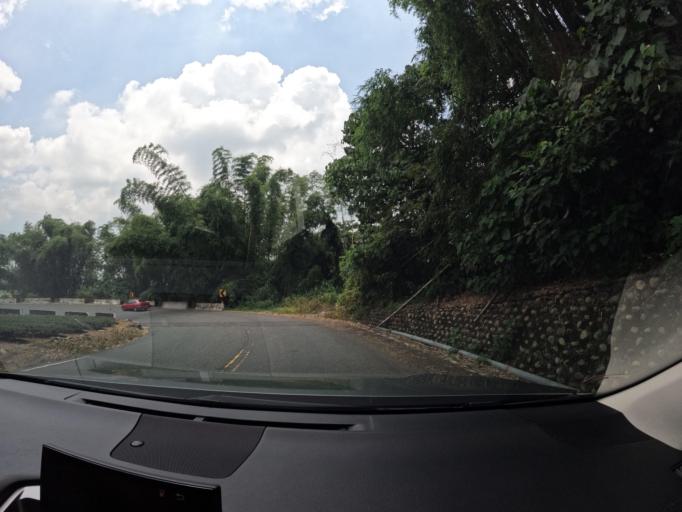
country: TW
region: Taiwan
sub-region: Nantou
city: Nantou
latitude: 23.8869
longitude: 120.6307
